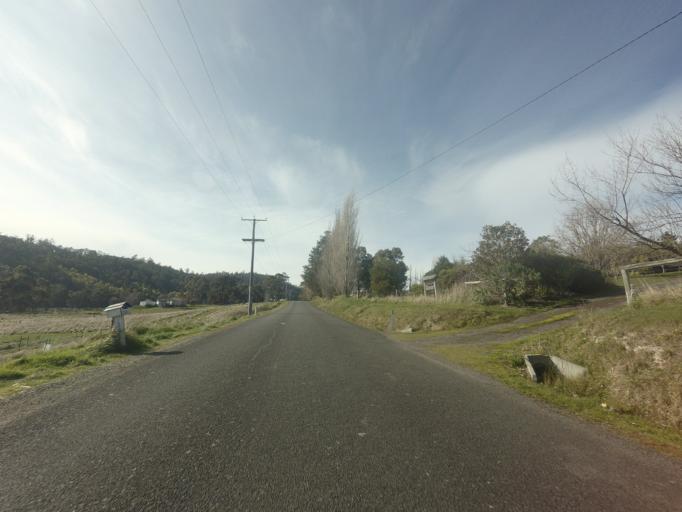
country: AU
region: Tasmania
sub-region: Huon Valley
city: Cygnet
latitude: -43.1815
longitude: 147.1244
